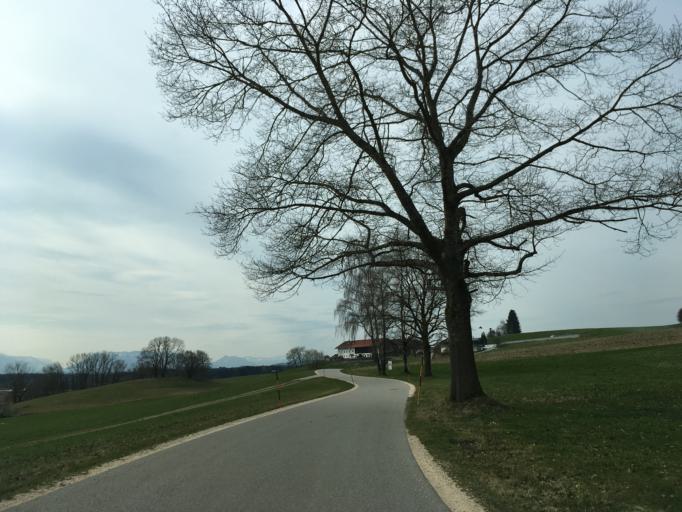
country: DE
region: Bavaria
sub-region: Upper Bavaria
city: Pittenhart
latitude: 47.9551
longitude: 12.4040
